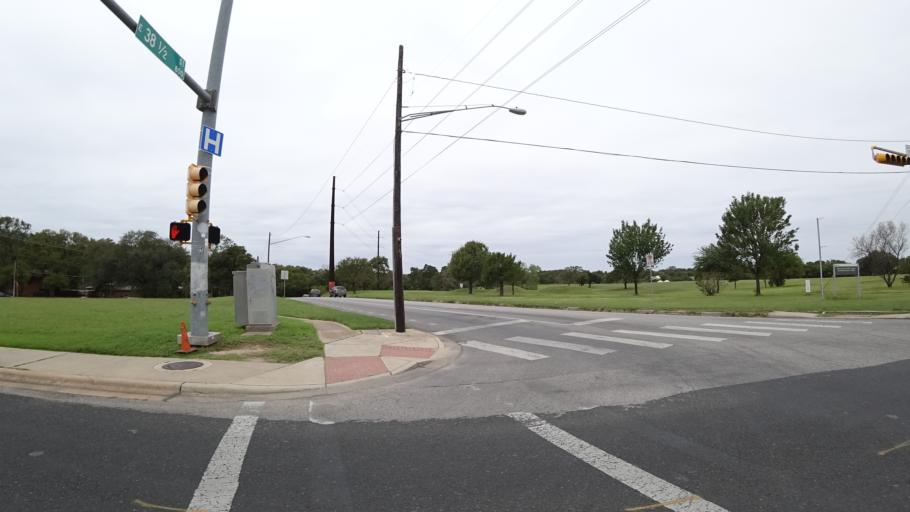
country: US
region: Texas
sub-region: Travis County
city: Austin
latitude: 30.2965
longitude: -97.7232
